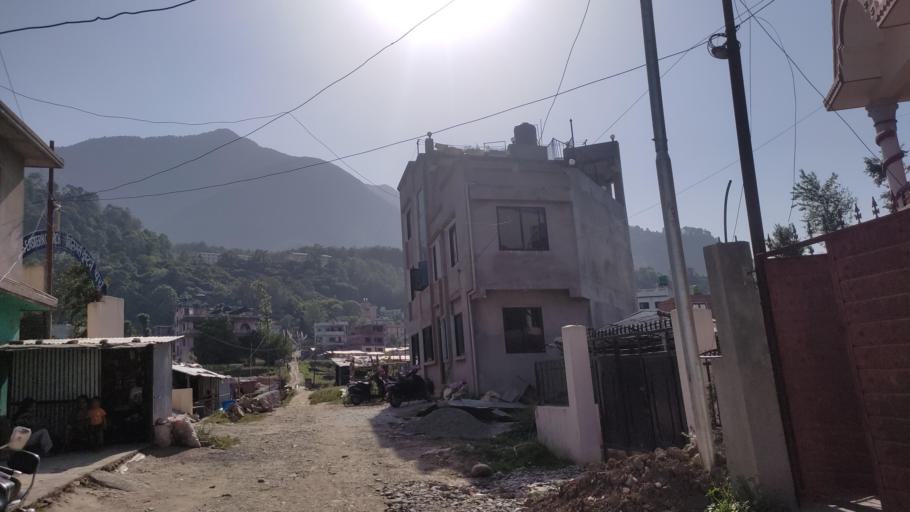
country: NP
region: Central Region
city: Kirtipur
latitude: 27.6628
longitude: 85.2621
